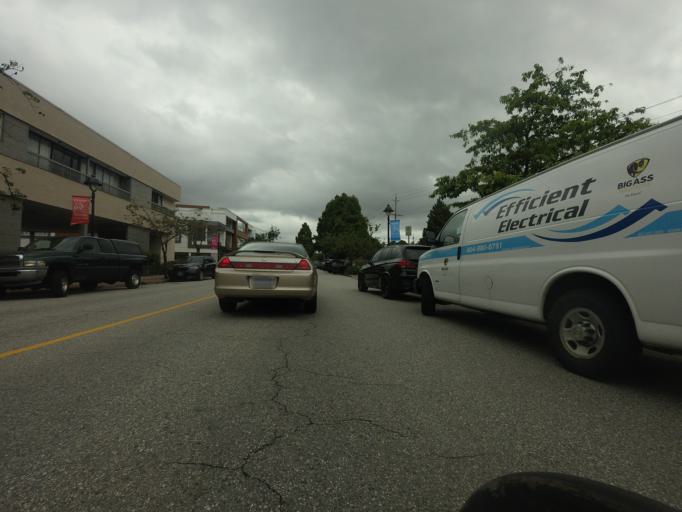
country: CA
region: British Columbia
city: West Vancouver
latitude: 49.3276
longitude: -123.1581
